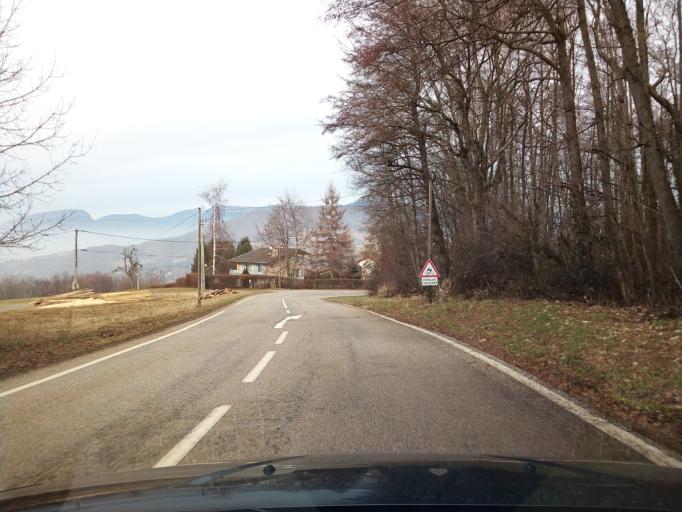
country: FR
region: Rhone-Alpes
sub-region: Departement de l'Isere
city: Revel
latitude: 45.1445
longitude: 5.8554
